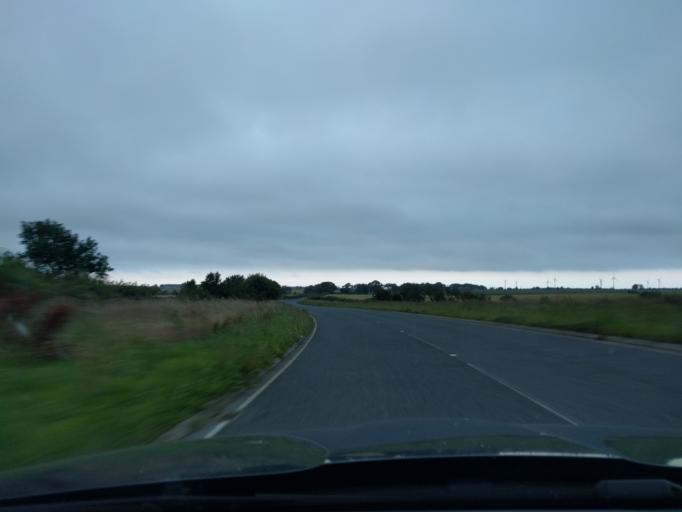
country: GB
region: England
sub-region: Northumberland
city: Felton
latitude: 55.2530
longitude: -1.6752
